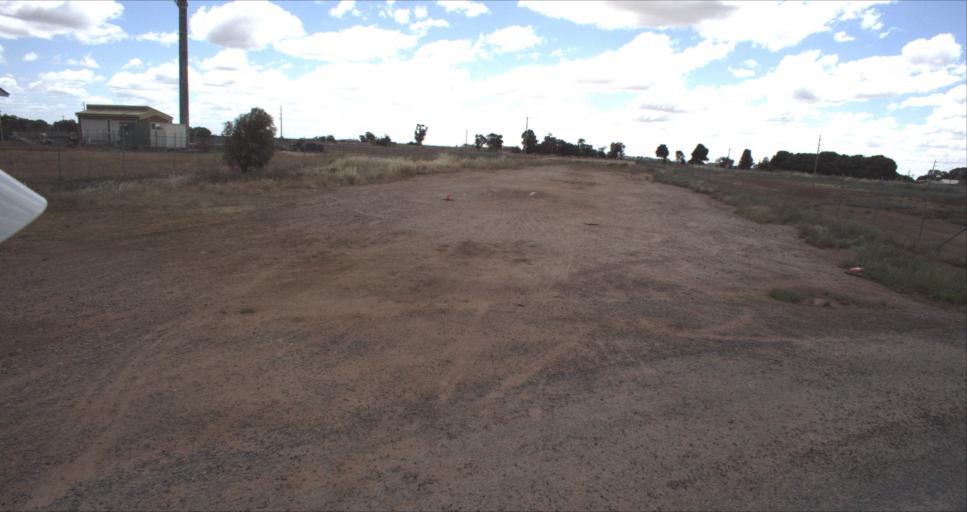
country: AU
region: New South Wales
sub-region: Murrumbidgee Shire
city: Darlington Point
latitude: -34.5140
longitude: 146.1828
